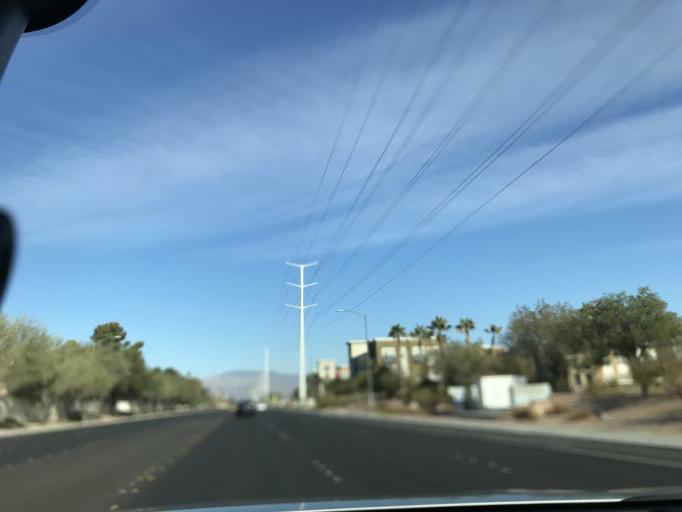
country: US
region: Nevada
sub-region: Clark County
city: Spring Valley
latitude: 36.2075
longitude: -115.2605
